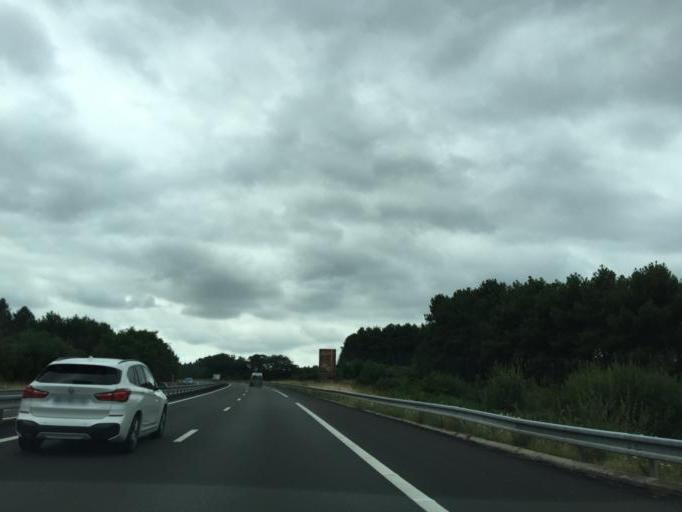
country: FR
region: Pays de la Loire
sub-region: Departement de la Sarthe
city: Teloche
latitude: 47.8583
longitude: 0.2975
